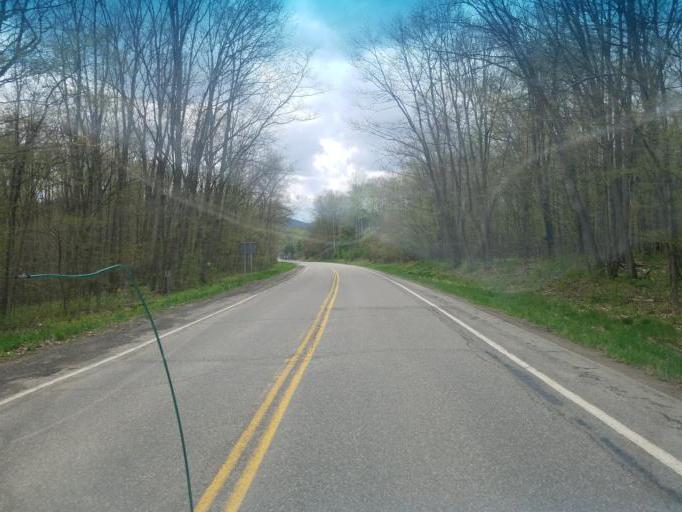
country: US
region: New York
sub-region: Allegany County
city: Wellsville
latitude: 42.0007
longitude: -77.8608
